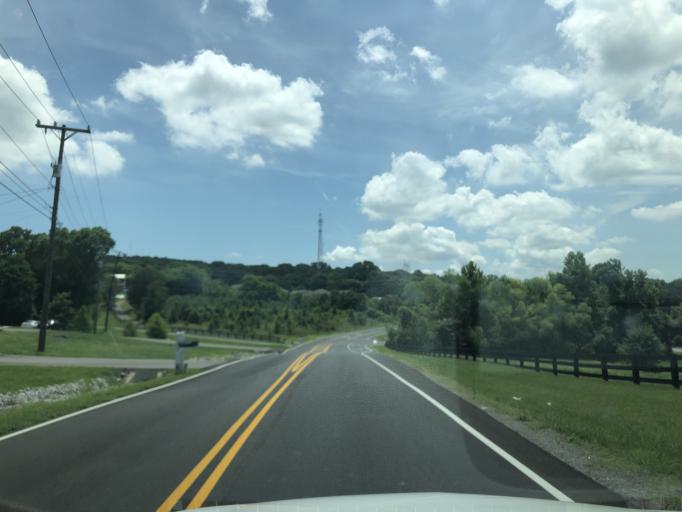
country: US
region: Tennessee
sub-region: Rutherford County
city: La Vergne
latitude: 36.0235
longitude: -86.6452
